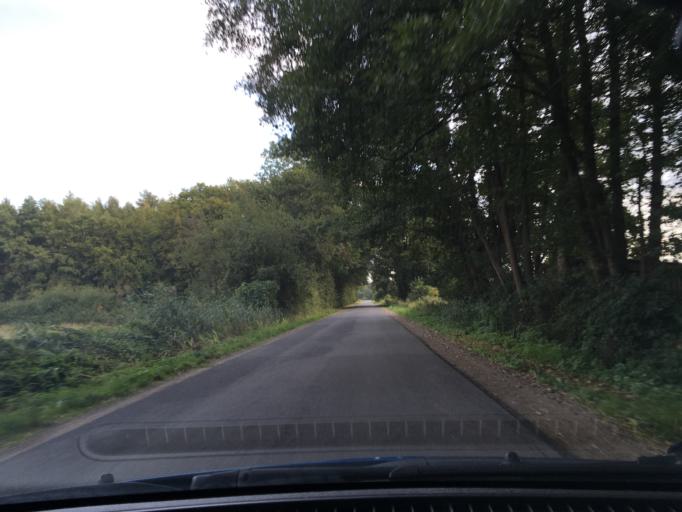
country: DE
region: Lower Saxony
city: Garstedt
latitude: 53.2828
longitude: 10.1713
